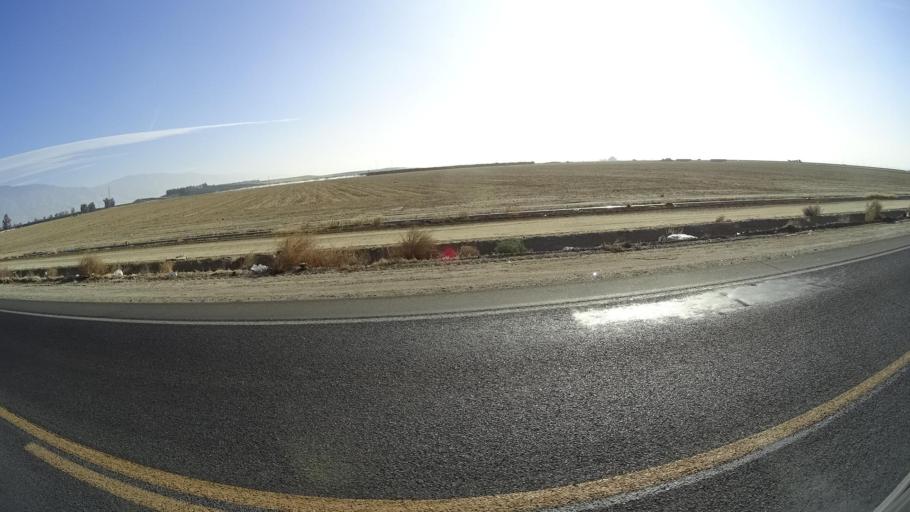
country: US
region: California
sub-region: Kern County
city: Arvin
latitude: 35.3299
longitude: -118.7957
